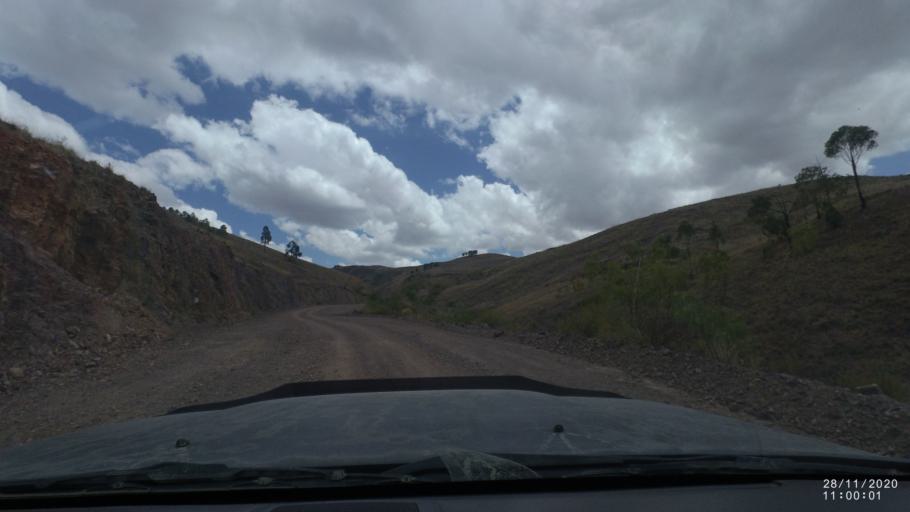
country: BO
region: Cochabamba
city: Capinota
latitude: -17.7715
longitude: -66.1075
